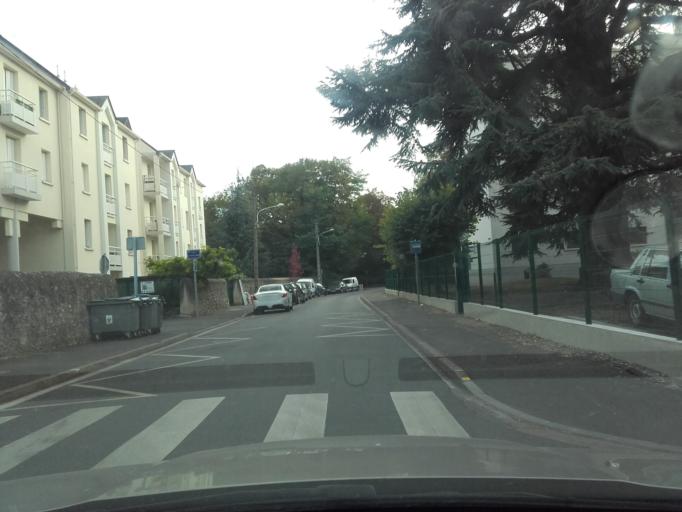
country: FR
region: Centre
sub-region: Departement d'Indre-et-Loire
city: Saint-Cyr-sur-Loire
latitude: 47.4097
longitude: 0.6918
